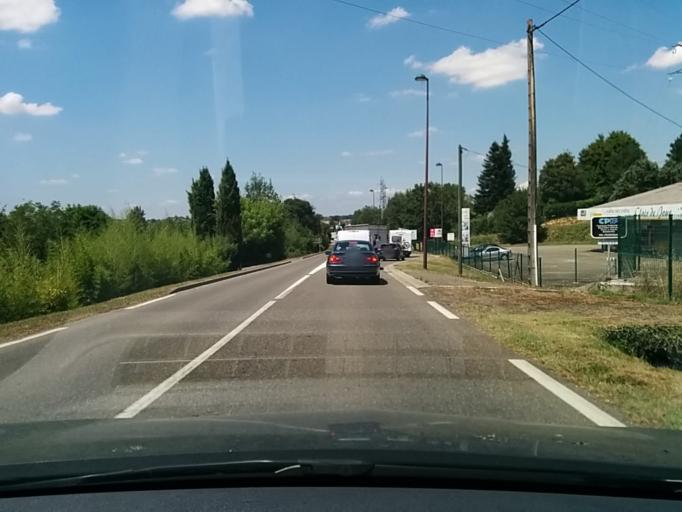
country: FR
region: Midi-Pyrenees
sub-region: Departement du Gers
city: Vic-Fezensac
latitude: 43.7519
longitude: 0.3137
